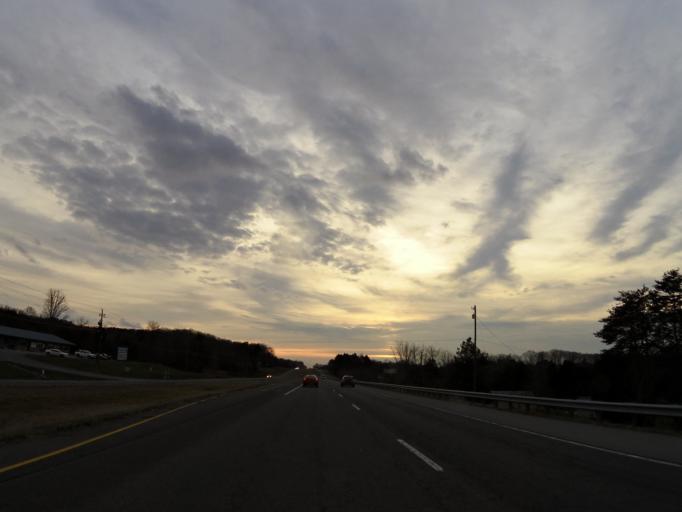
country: US
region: Tennessee
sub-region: Monroe County
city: Madisonville
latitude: 35.5549
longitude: -84.3076
